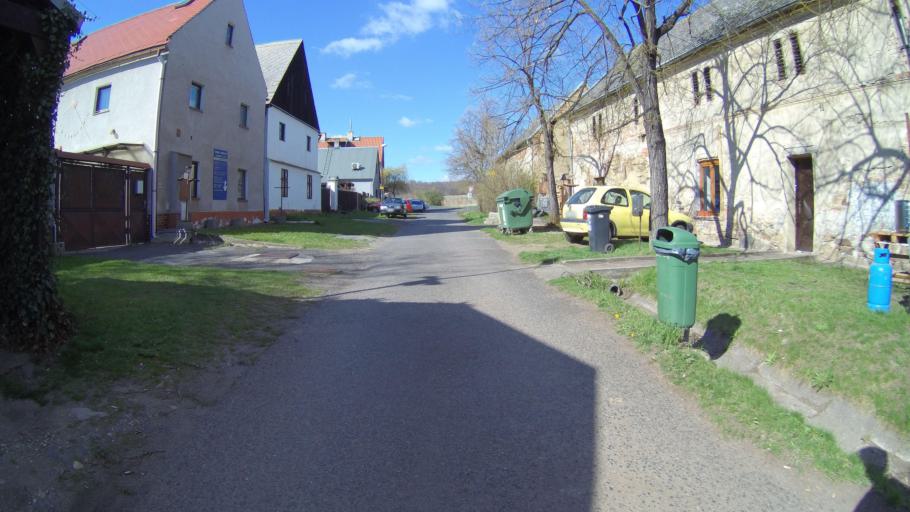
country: CZ
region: Ustecky
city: Brezno
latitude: 50.3704
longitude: 13.4342
